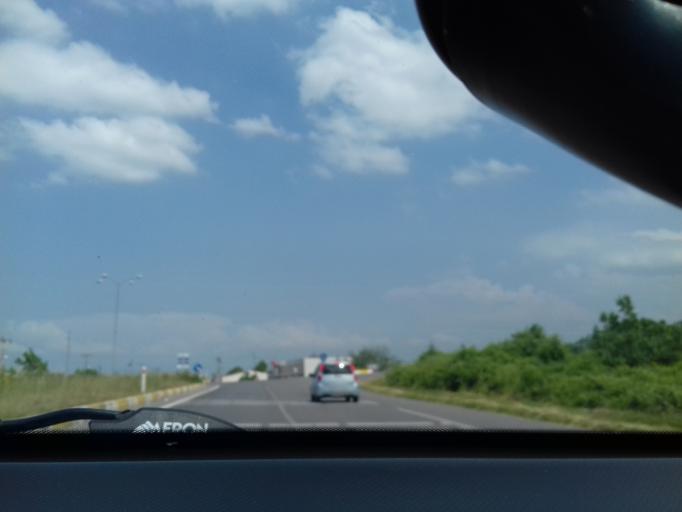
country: TR
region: Sakarya
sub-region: Merkez
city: Sapanca
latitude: 40.7135
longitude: 30.3448
